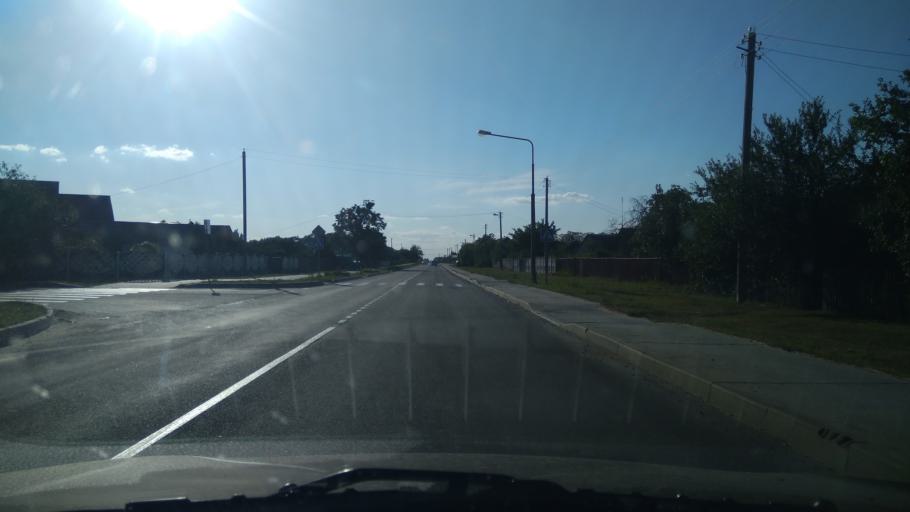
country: BY
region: Brest
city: Byaroza
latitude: 52.5431
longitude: 24.9687
